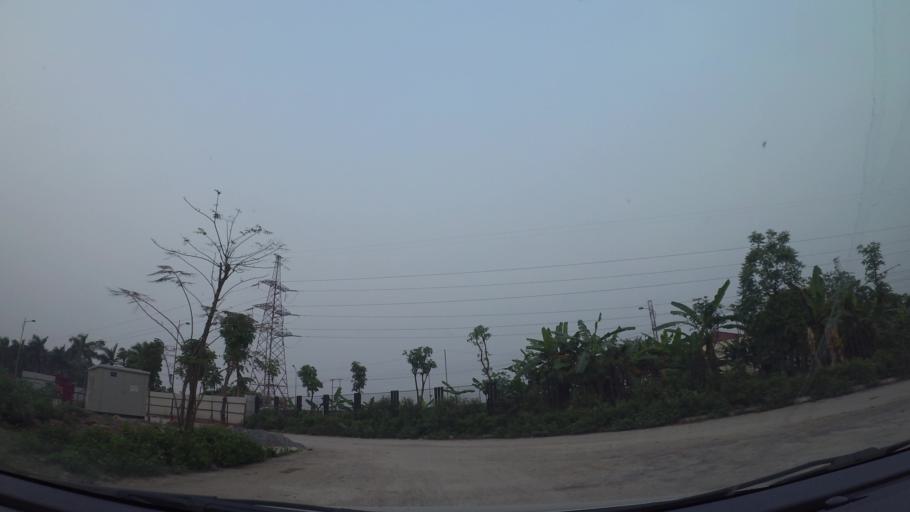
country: VN
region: Ha Noi
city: Ha Dong
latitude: 20.9956
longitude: 105.7345
